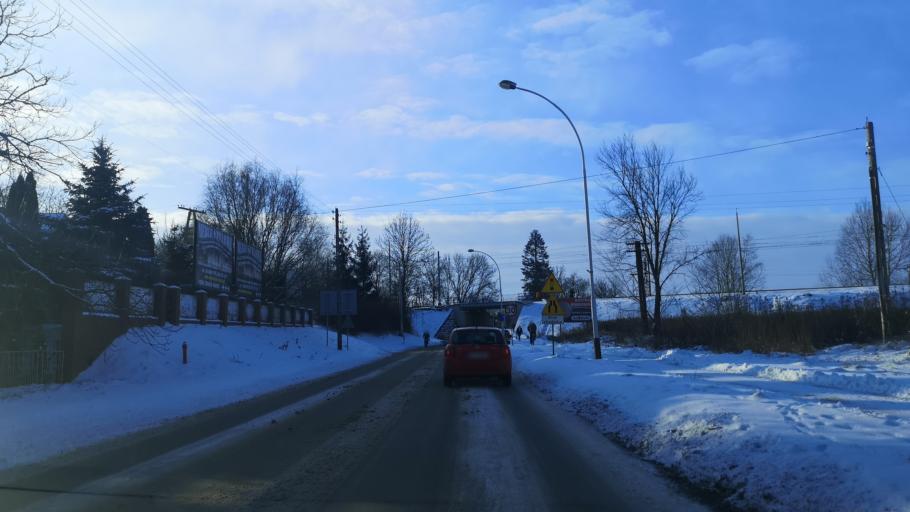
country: PL
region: Subcarpathian Voivodeship
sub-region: Powiat przeworski
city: Przeworsk
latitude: 50.0724
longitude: 22.4911
